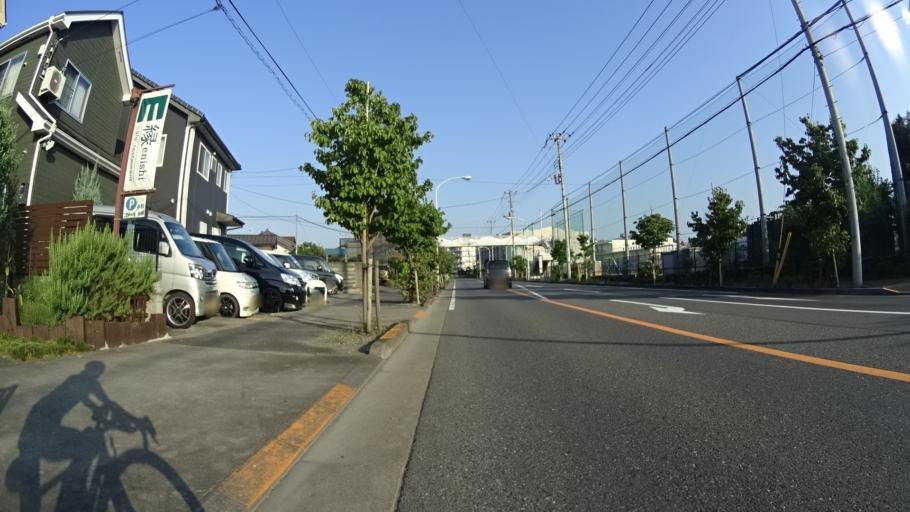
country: JP
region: Tokyo
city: Ome
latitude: 35.7793
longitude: 139.2716
